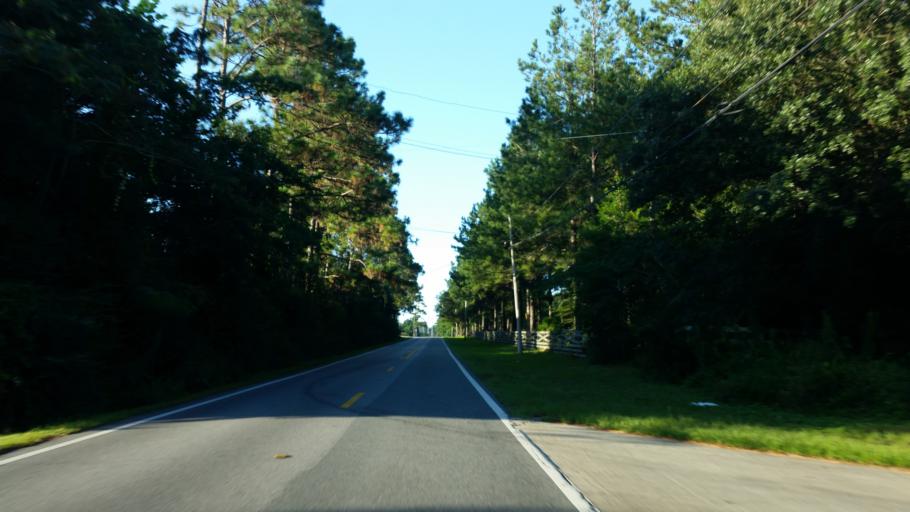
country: US
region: Florida
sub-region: Escambia County
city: Bellview
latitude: 30.5020
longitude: -87.3312
